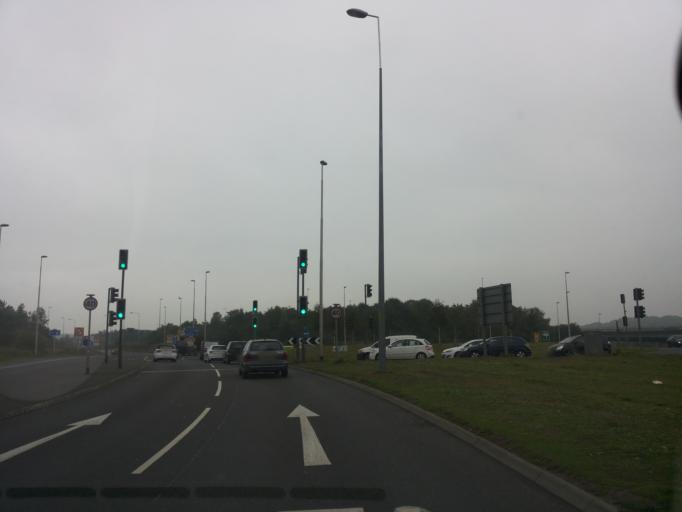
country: GB
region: England
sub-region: Lancashire
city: Goosnargh
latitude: 53.7653
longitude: -2.6326
